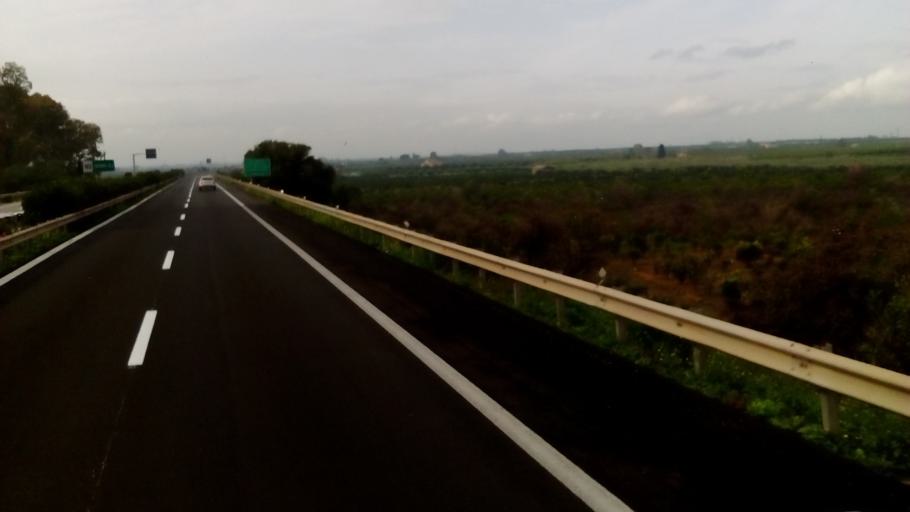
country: IT
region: Sicily
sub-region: Catania
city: Motta Sant'Anastasia
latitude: 37.4644
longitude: 14.9319
